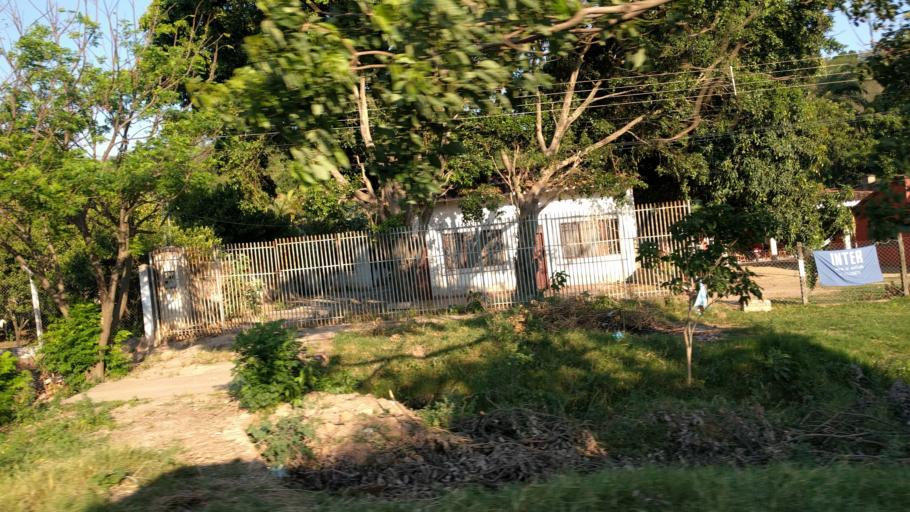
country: BO
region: Santa Cruz
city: Limoncito
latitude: -18.0129
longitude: -63.3940
